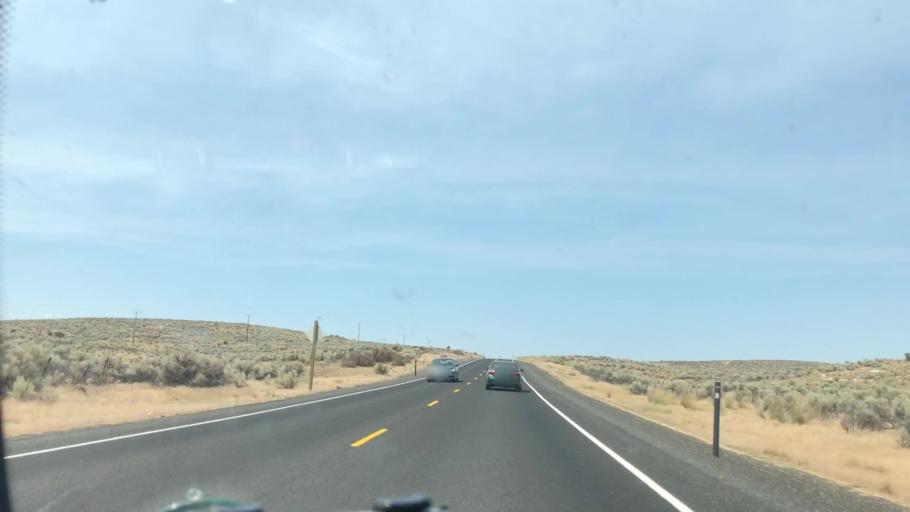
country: US
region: Idaho
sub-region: Owyhee County
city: Murphy
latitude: 42.9891
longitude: -117.0569
